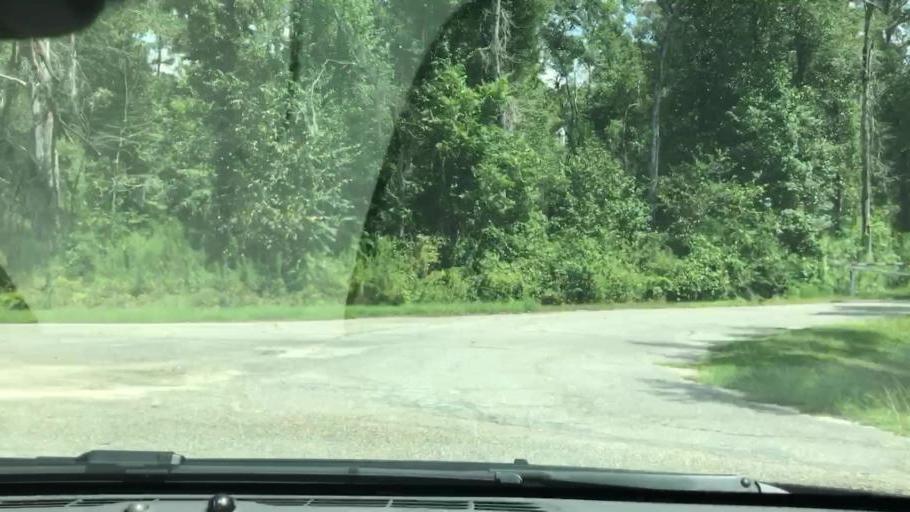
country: US
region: Georgia
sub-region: Quitman County
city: Georgetown
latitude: 32.0247
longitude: -85.0373
